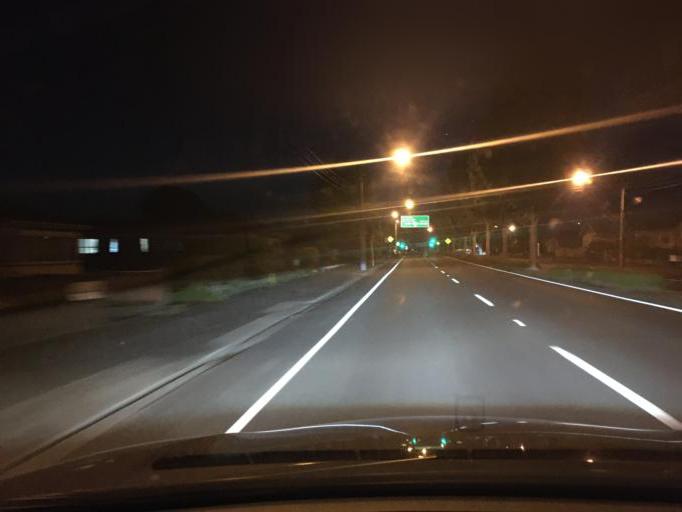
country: NZ
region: Waikato
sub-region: Hamilton City
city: Hamilton
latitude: -37.8107
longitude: 175.2845
